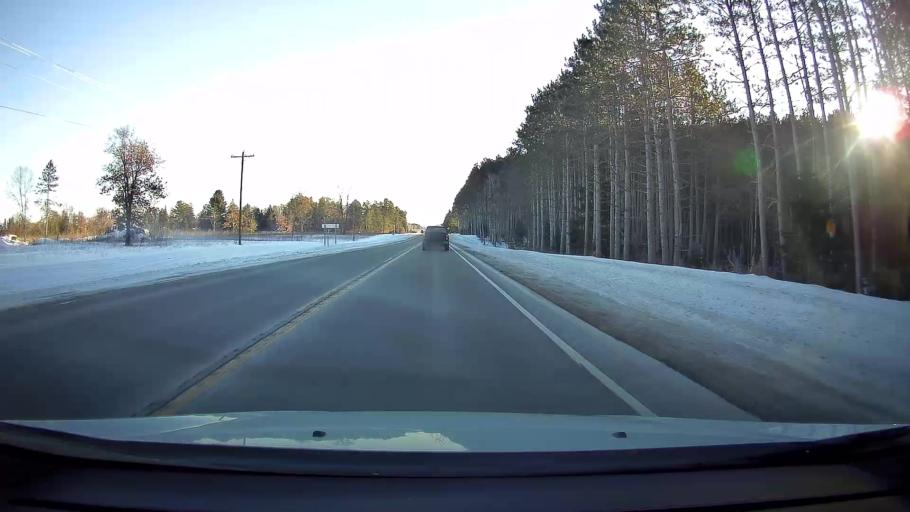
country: US
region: Wisconsin
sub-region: Sawyer County
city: Hayward
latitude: 45.9976
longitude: -91.6233
